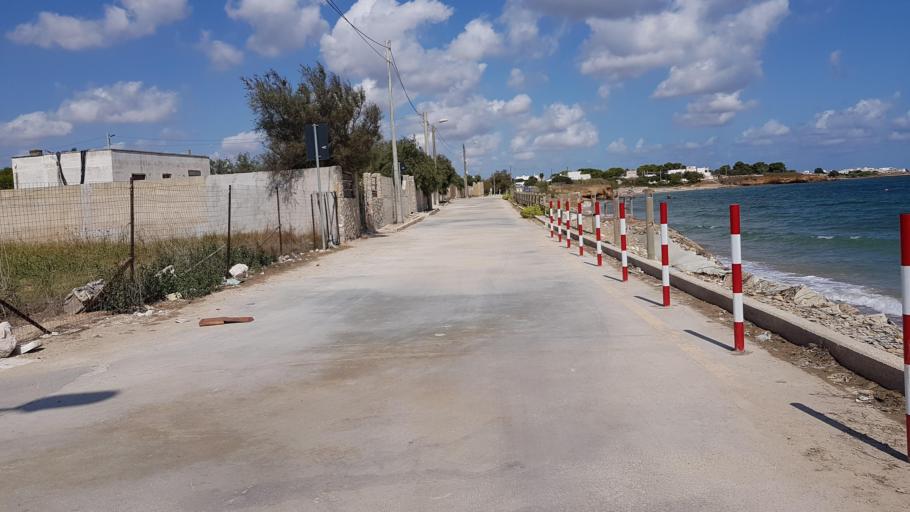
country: IT
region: Apulia
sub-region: Provincia di Brindisi
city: Torchiarolo
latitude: 40.5249
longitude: 18.0812
